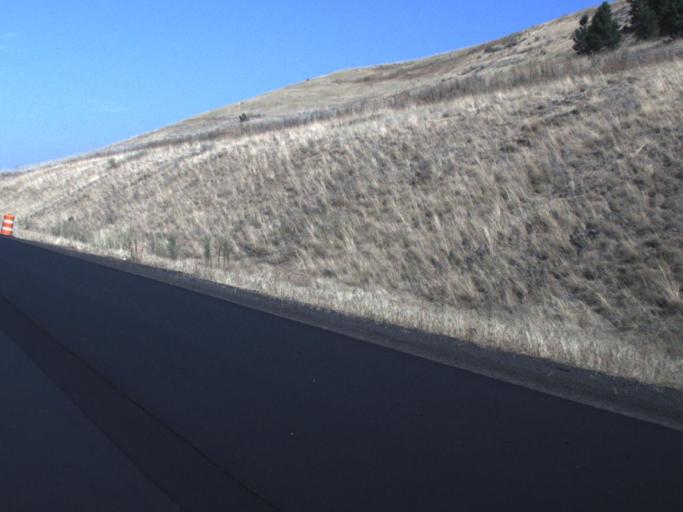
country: US
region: Washington
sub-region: Spokane County
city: Medical Lake
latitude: 47.3653
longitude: -117.8842
